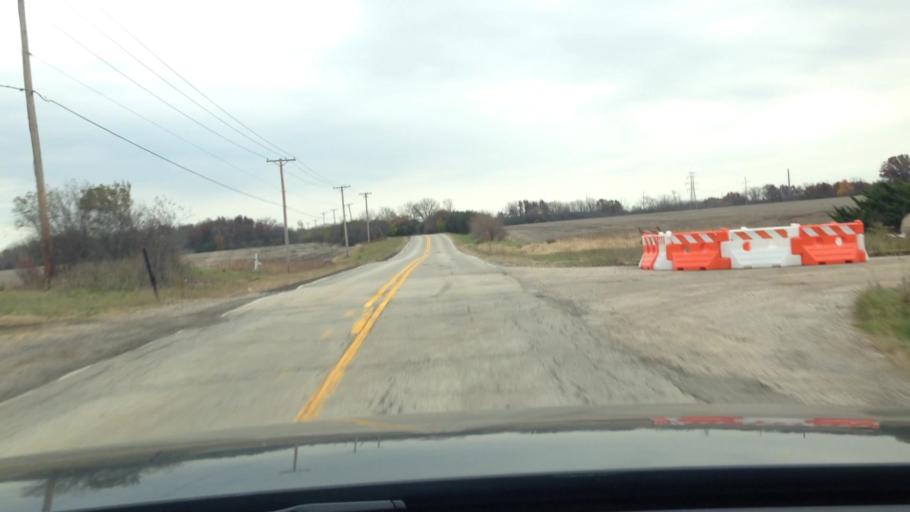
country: US
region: Illinois
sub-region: McHenry County
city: Woodstock
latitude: 42.2725
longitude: -88.4440
